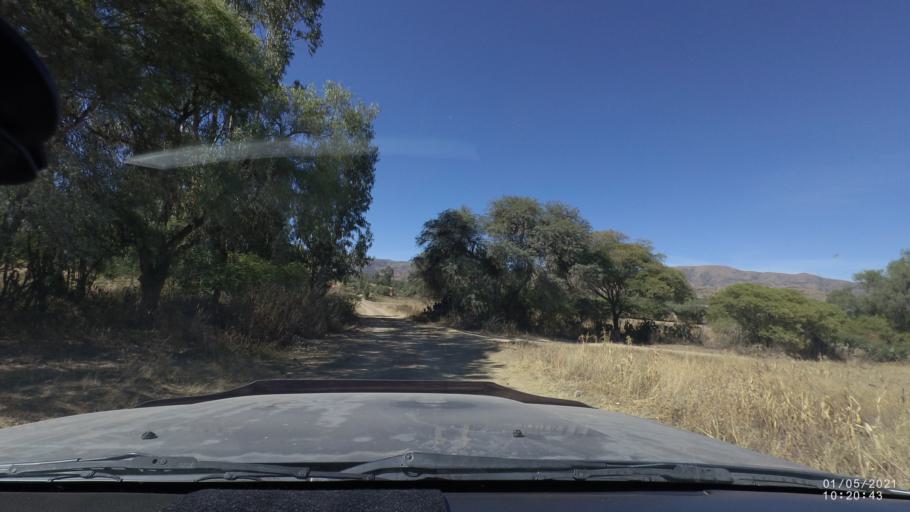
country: BO
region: Cochabamba
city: Capinota
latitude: -17.5623
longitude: -66.2039
